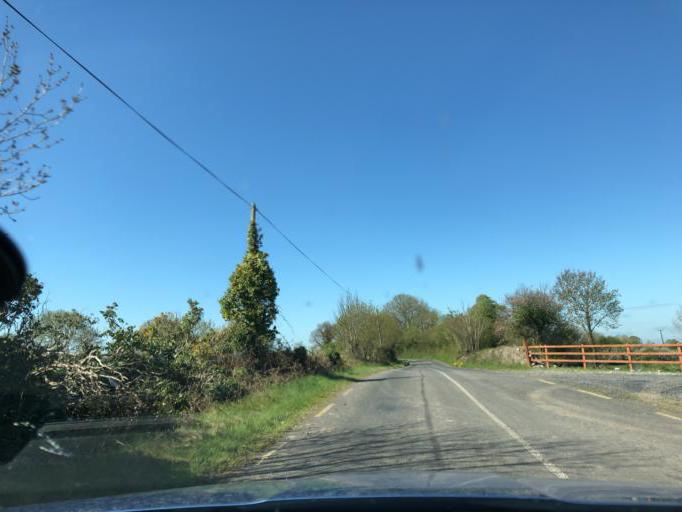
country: IE
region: Connaught
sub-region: County Galway
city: Portumna
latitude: 53.1622
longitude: -8.2429
